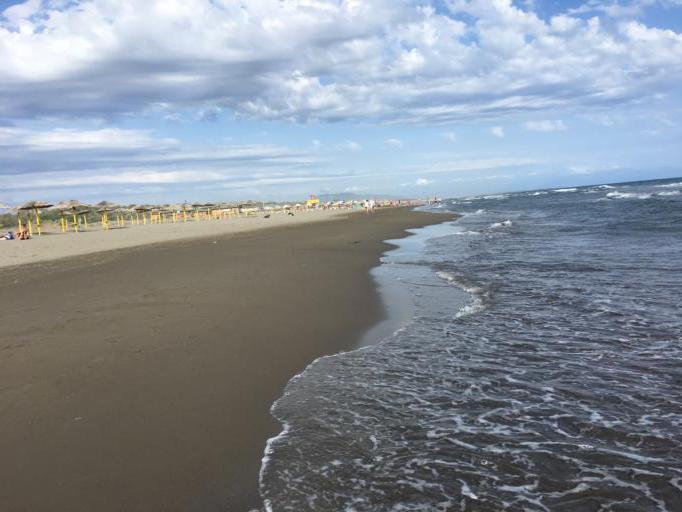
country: ME
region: Ulcinj
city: Ulcinj
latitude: 41.9077
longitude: 19.2460
